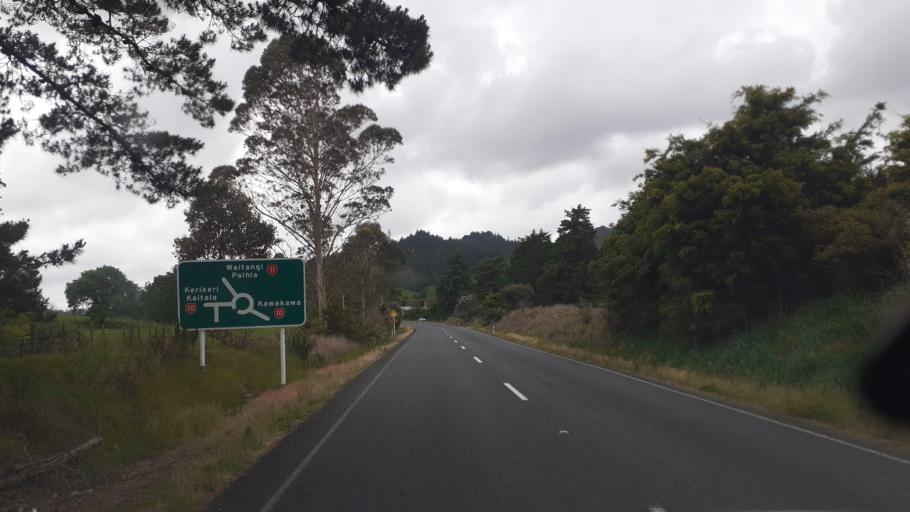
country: NZ
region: Northland
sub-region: Far North District
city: Waimate North
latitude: -35.3030
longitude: 173.9566
